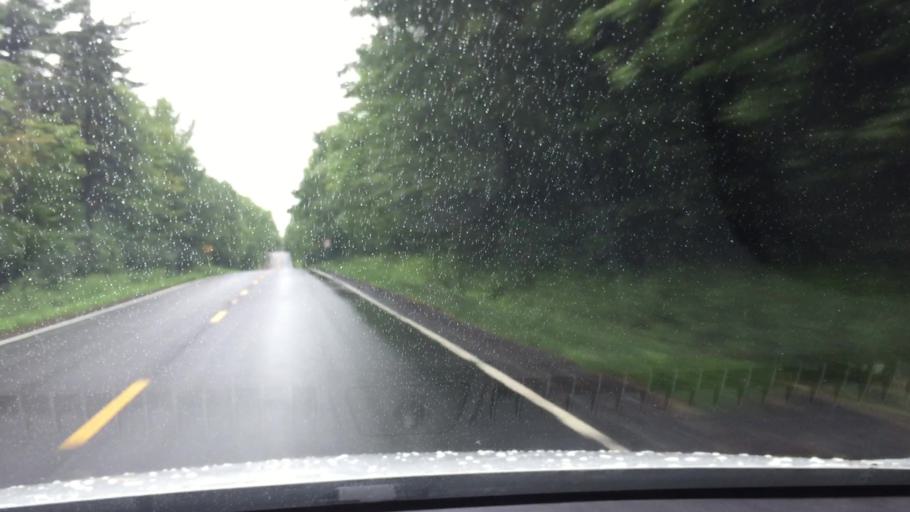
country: US
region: Massachusetts
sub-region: Berkshire County
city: Hinsdale
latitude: 42.3824
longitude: -73.1553
